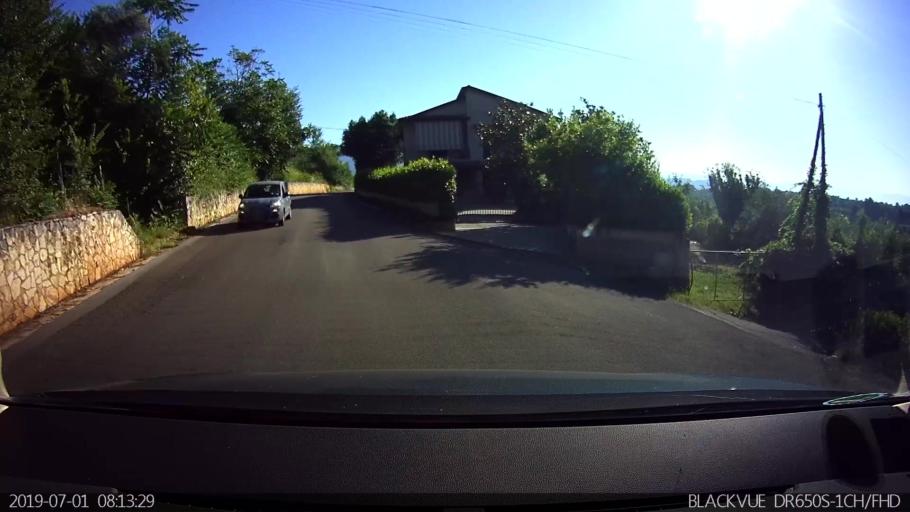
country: IT
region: Latium
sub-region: Provincia di Frosinone
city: Veroli
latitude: 41.6902
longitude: 13.4230
